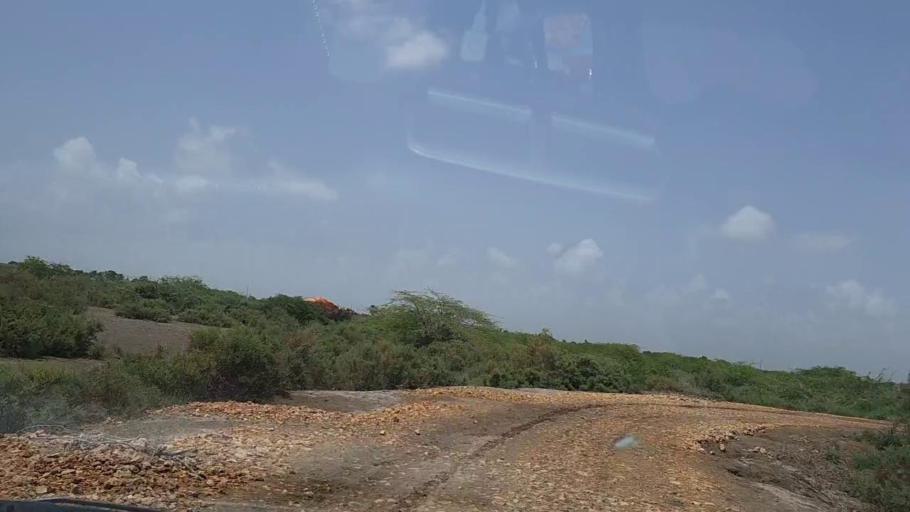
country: PK
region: Sindh
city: Keti Bandar
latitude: 24.1521
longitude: 67.5371
